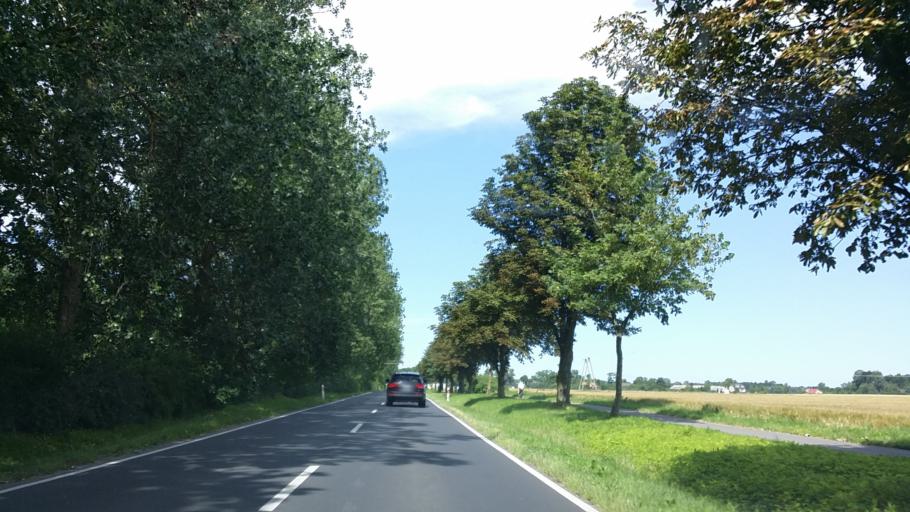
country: PL
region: West Pomeranian Voivodeship
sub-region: Powiat koszalinski
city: Mielno
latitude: 54.2330
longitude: 16.0733
